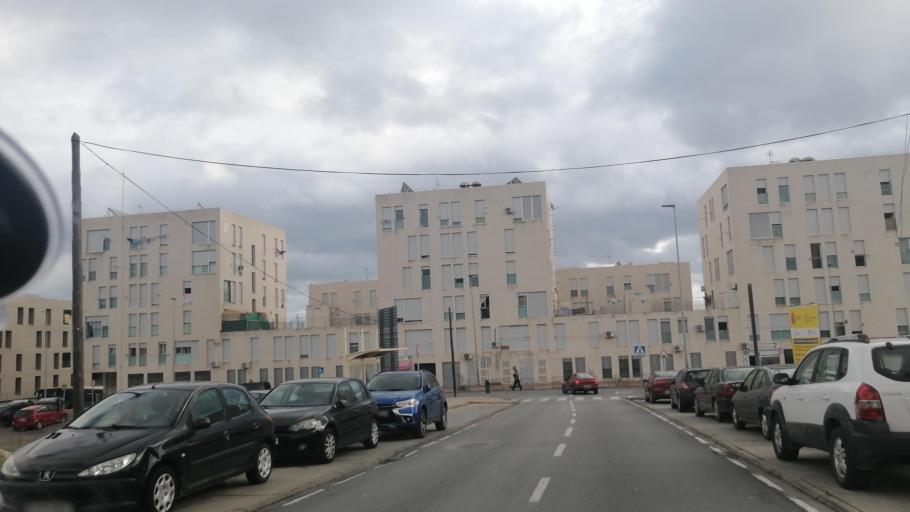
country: ES
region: Ceuta
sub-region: Ceuta
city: Ceuta
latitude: 35.8813
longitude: -5.3437
